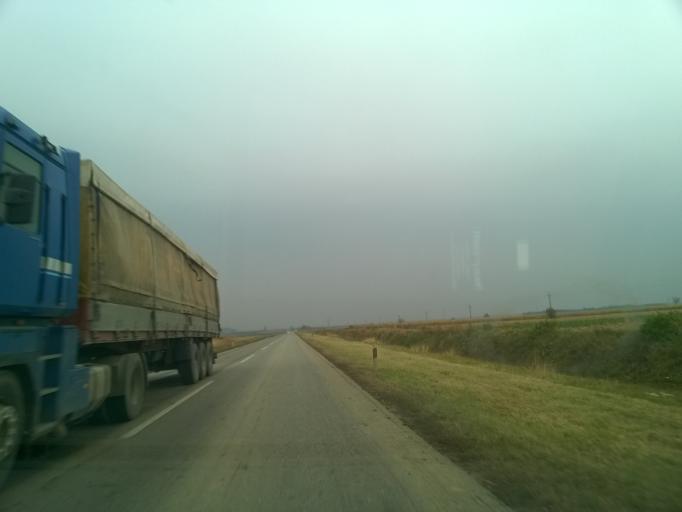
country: RS
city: Debeljaca
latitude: 45.0582
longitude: 20.6399
